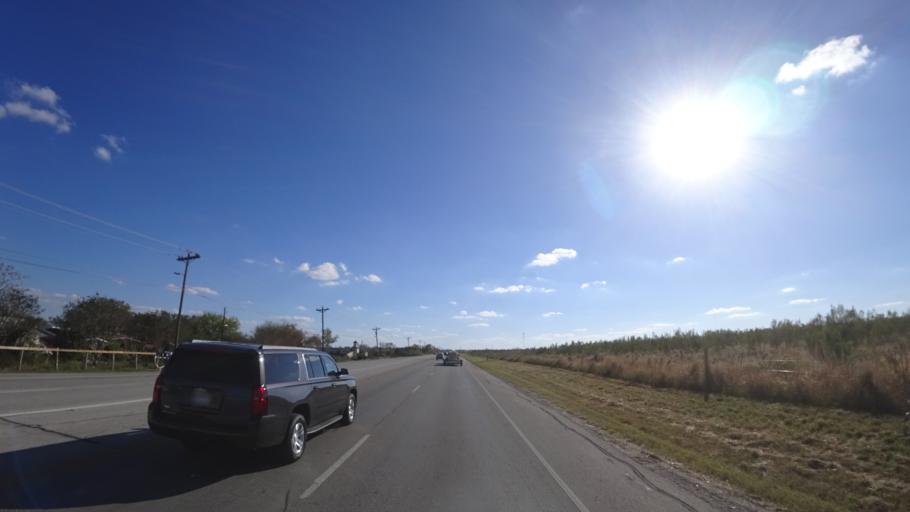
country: US
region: Texas
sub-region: Travis County
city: Onion Creek
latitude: 30.1433
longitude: -97.6968
